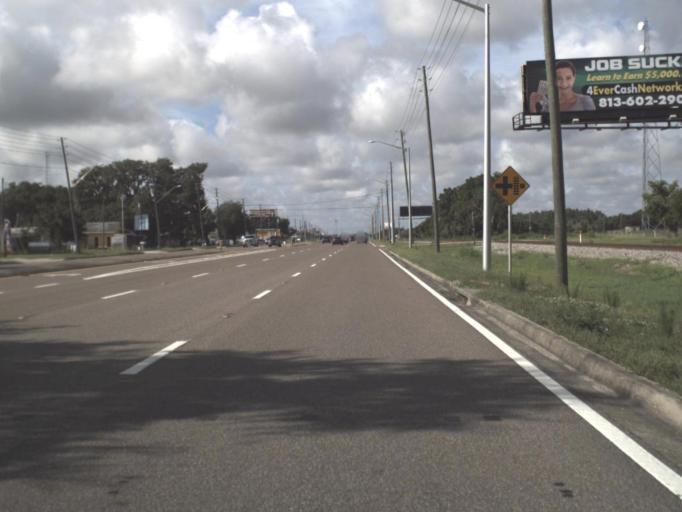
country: US
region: Florida
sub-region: Pasco County
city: Land O' Lakes
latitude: 28.1996
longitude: -82.4642
